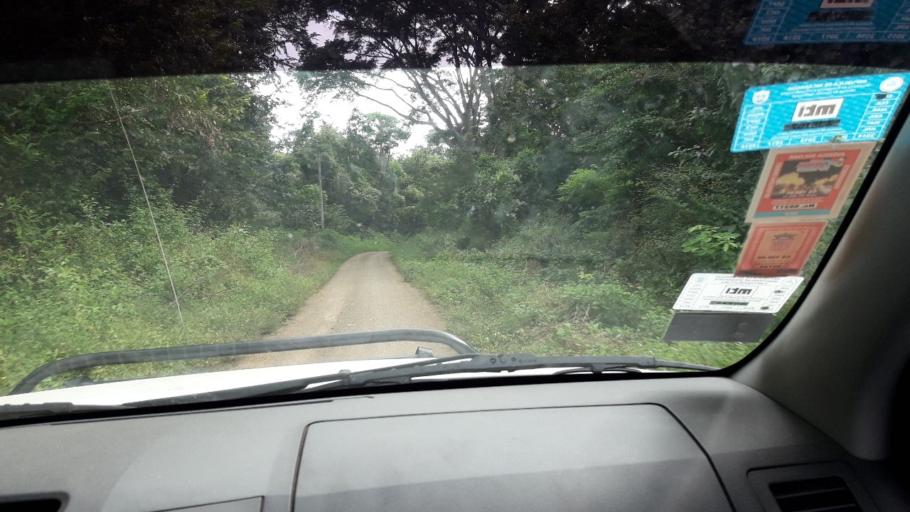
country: NI
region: Rivas
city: San Juan del Sur
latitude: 11.1885
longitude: -85.7845
